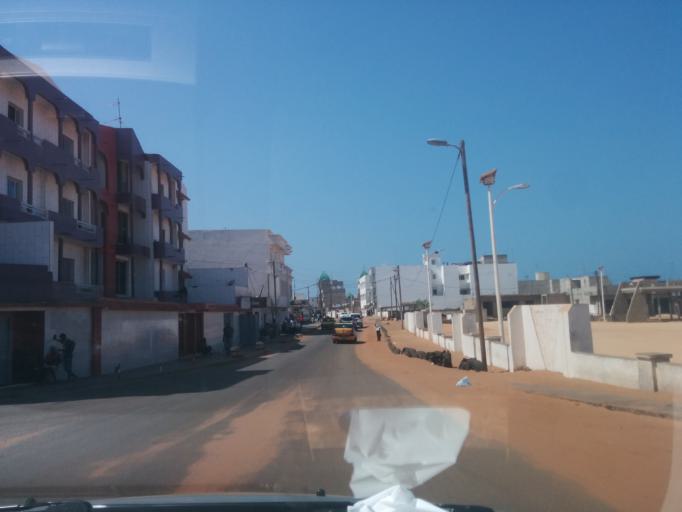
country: SN
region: Dakar
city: Pikine
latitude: 14.7708
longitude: -17.4266
